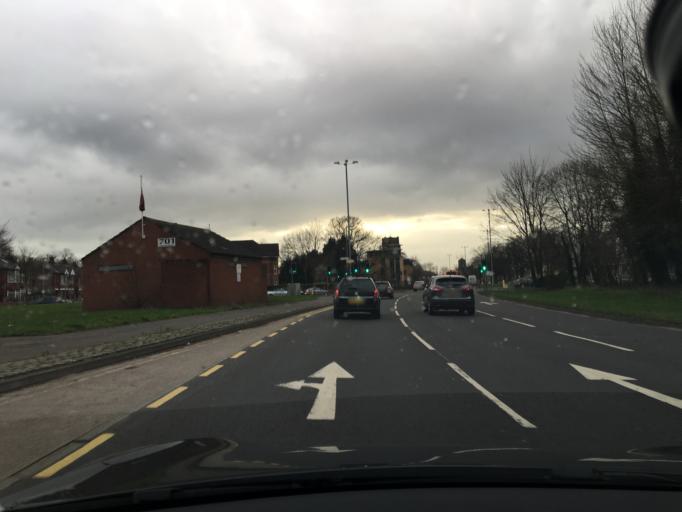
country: GB
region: England
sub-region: Manchester
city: Chorlton cum Hardy
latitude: 53.4256
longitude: -2.2543
